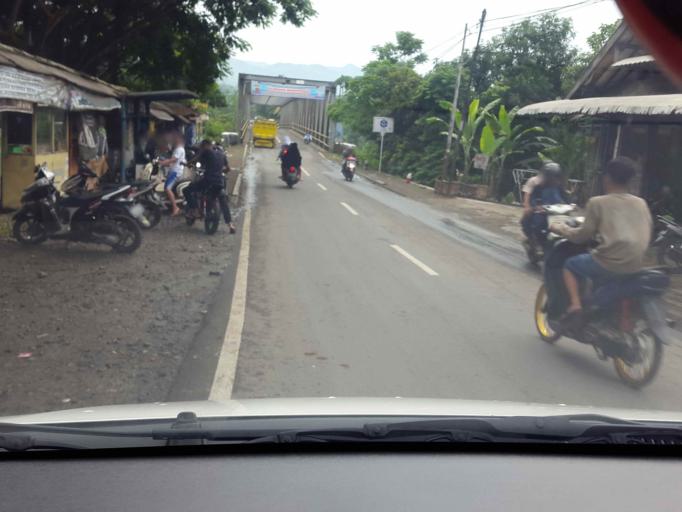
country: ID
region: West Java
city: Cidadap
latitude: -7.0112
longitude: 106.5669
